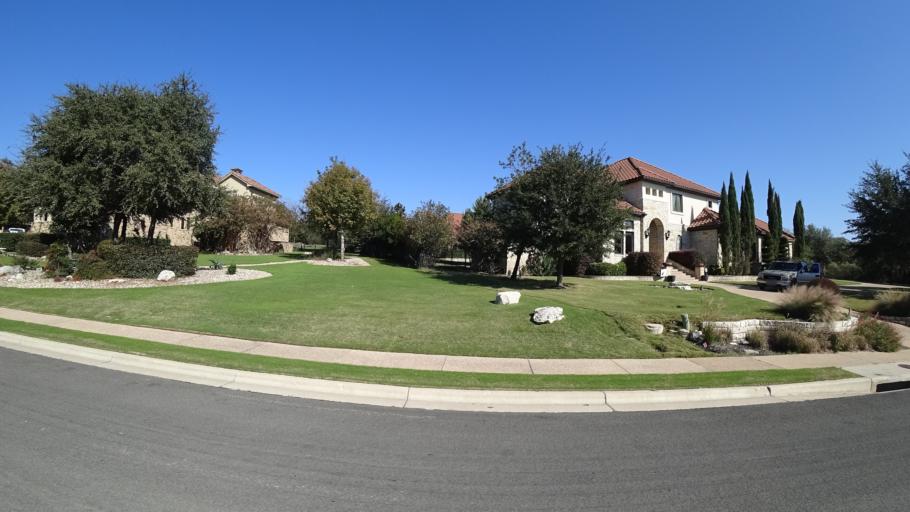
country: US
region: Texas
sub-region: Williamson County
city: Anderson Mill
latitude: 30.3845
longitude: -97.8465
